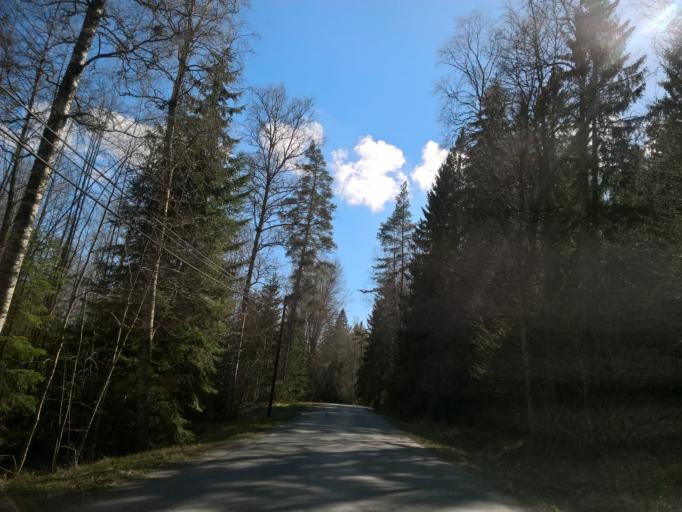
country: SE
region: OEstergoetland
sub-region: Finspangs Kommun
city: Finspang
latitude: 58.7231
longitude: 15.7600
